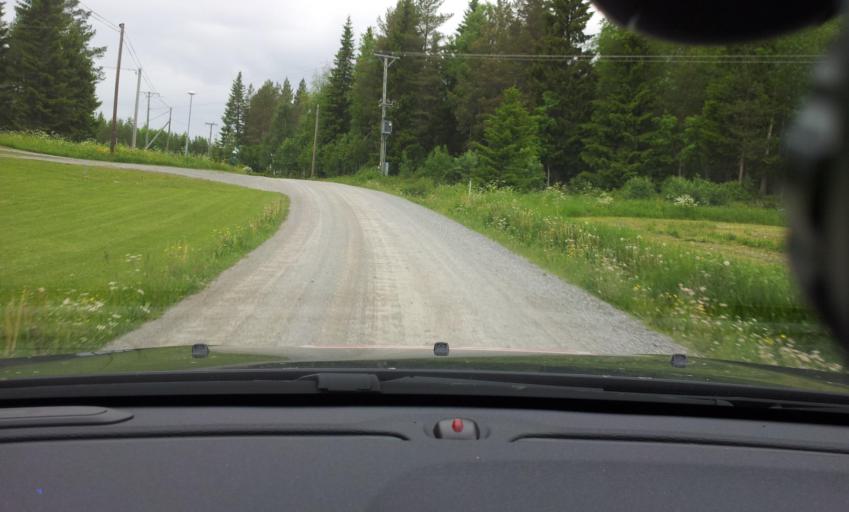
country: SE
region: Jaemtland
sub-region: OEstersunds Kommun
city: Brunflo
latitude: 62.9746
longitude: 14.6716
